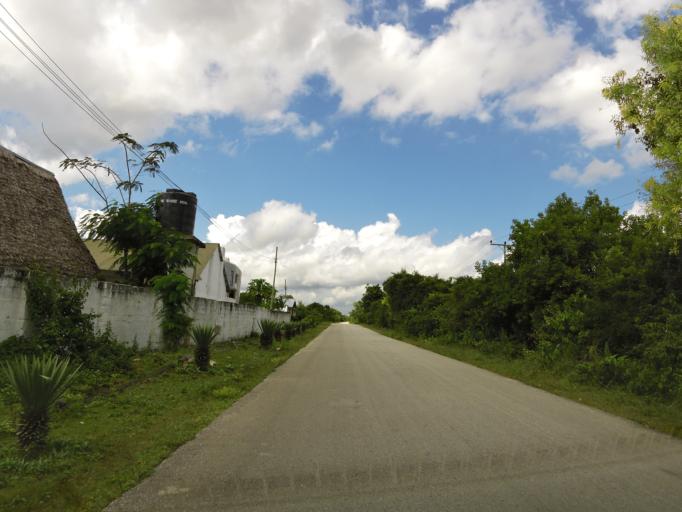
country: TZ
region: Zanzibar Central/South
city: Koani
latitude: -6.1434
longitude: 39.4267
